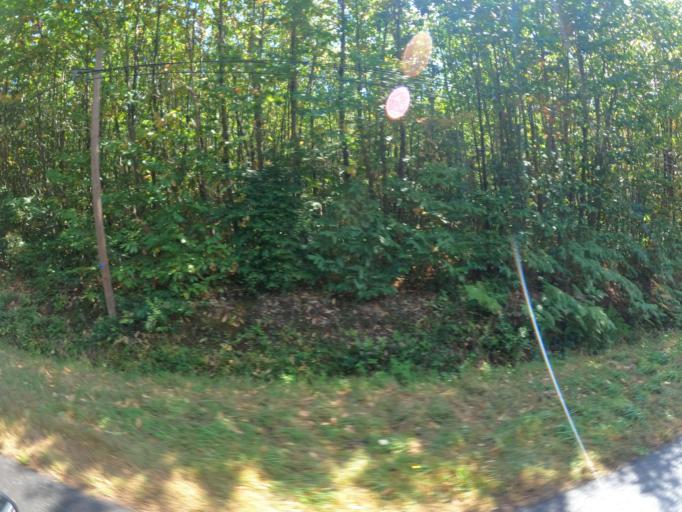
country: FR
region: Pays de la Loire
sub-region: Departement de Maine-et-Loire
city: Feneu
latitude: 47.6156
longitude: -0.5844
